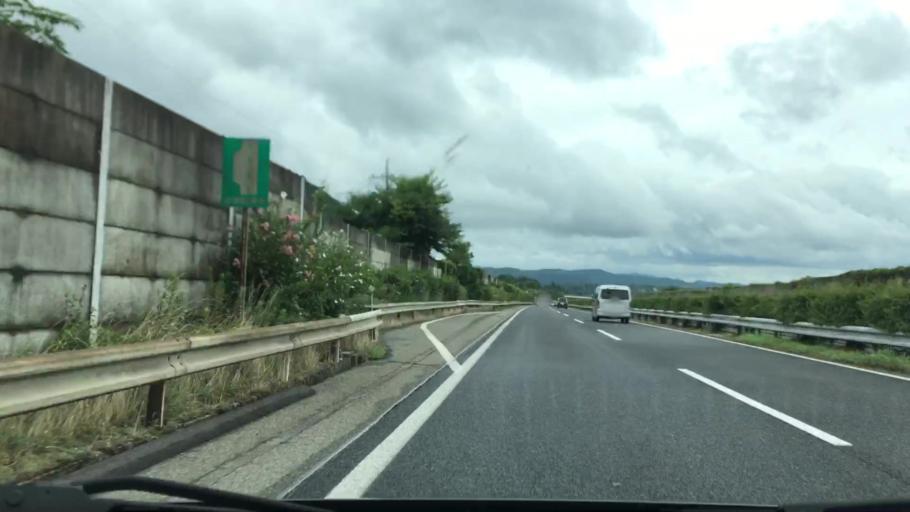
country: JP
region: Okayama
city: Tsuyama
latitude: 35.0226
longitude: 134.1869
